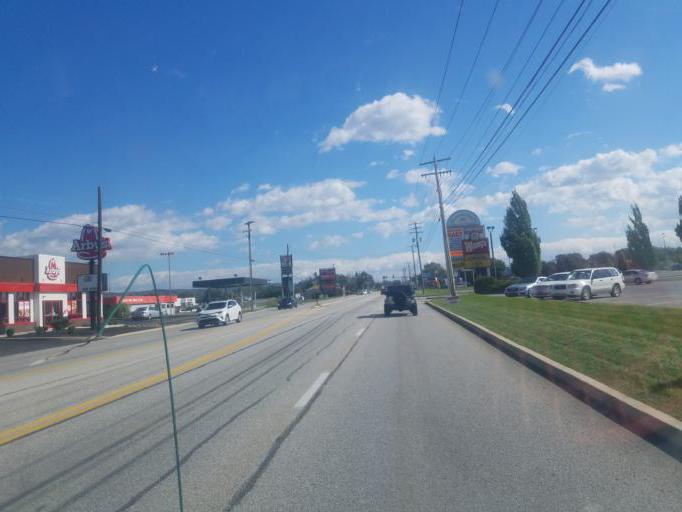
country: US
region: Pennsylvania
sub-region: Franklin County
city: Guilford
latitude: 39.9241
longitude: -77.6109
